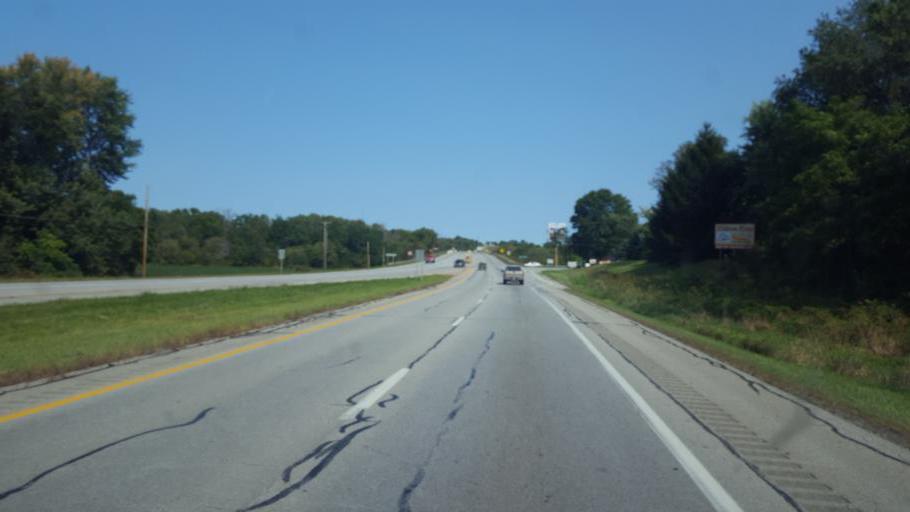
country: US
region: Ohio
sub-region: Wayne County
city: Orrville
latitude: 40.7968
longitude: -81.7483
